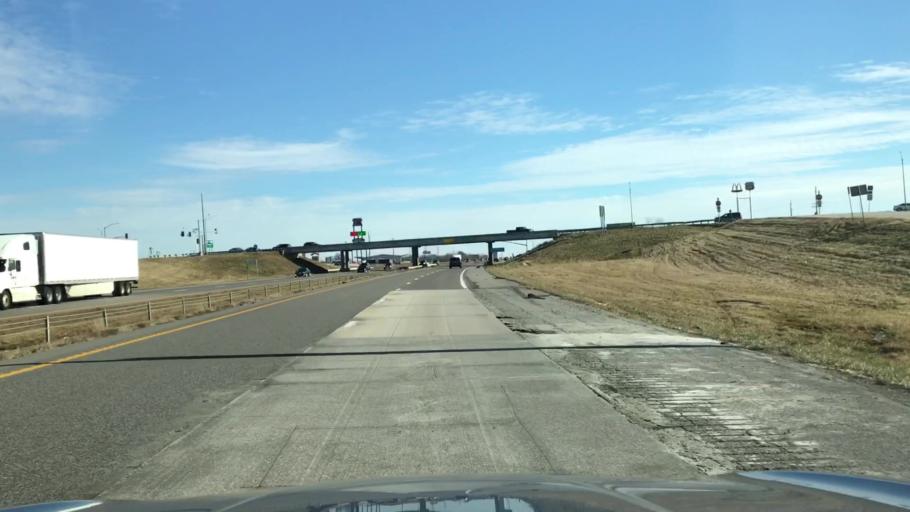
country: US
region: Missouri
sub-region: Warren County
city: Wright City
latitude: 38.8170
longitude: -90.9557
